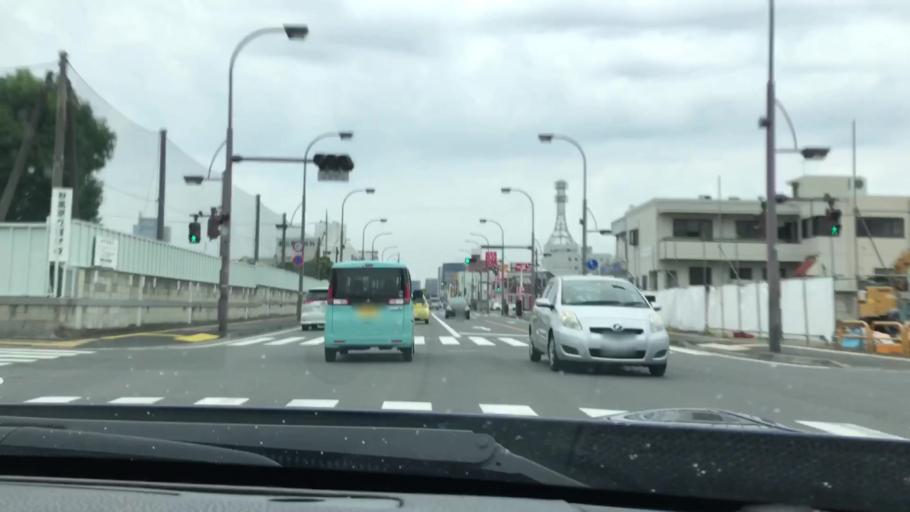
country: JP
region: Gunma
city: Maebashi-shi
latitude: 36.3772
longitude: 139.0700
